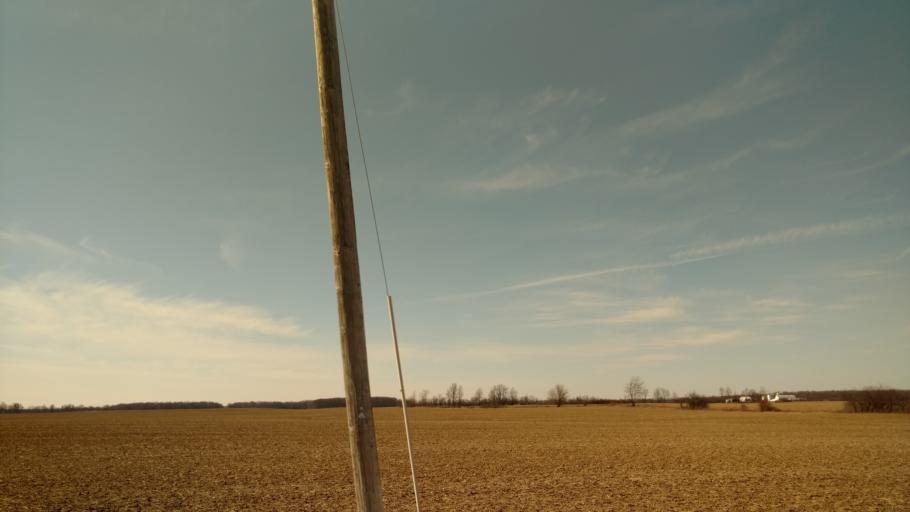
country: US
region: Ohio
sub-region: Union County
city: Richwood
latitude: 40.5219
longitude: -83.4537
